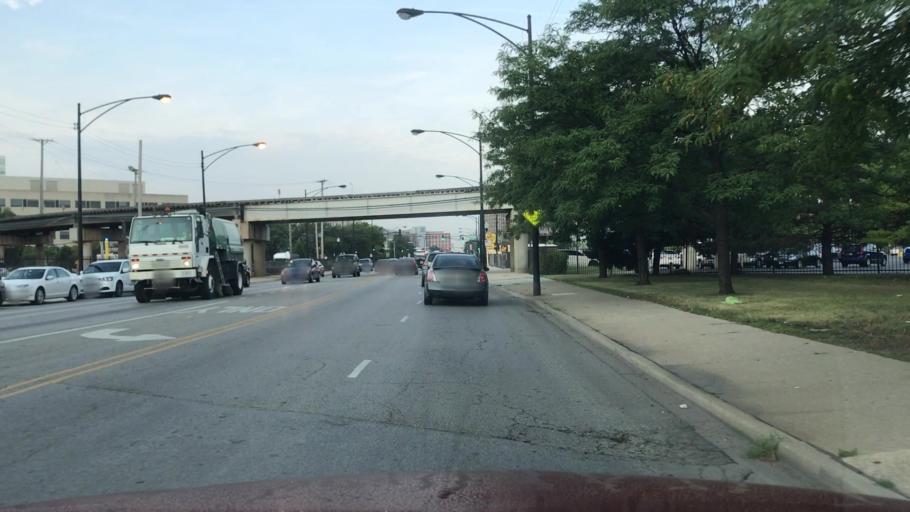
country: US
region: Illinois
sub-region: Cook County
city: Chicago
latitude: 41.8787
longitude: -87.6694
